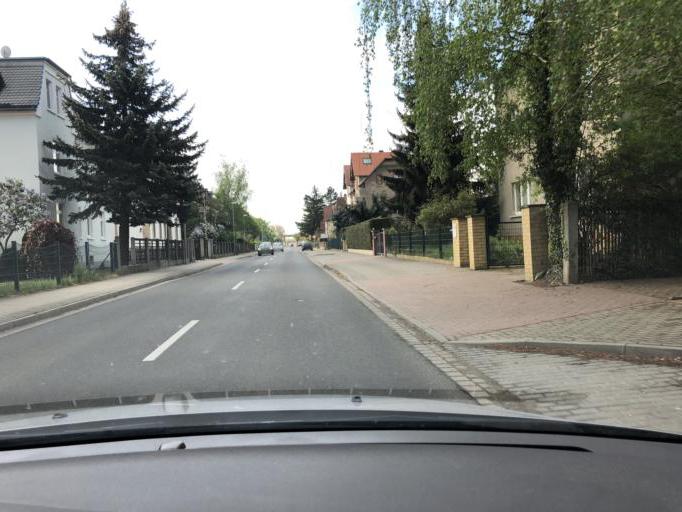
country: DE
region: Saxony
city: Bohlen
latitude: 51.2303
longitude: 12.3847
